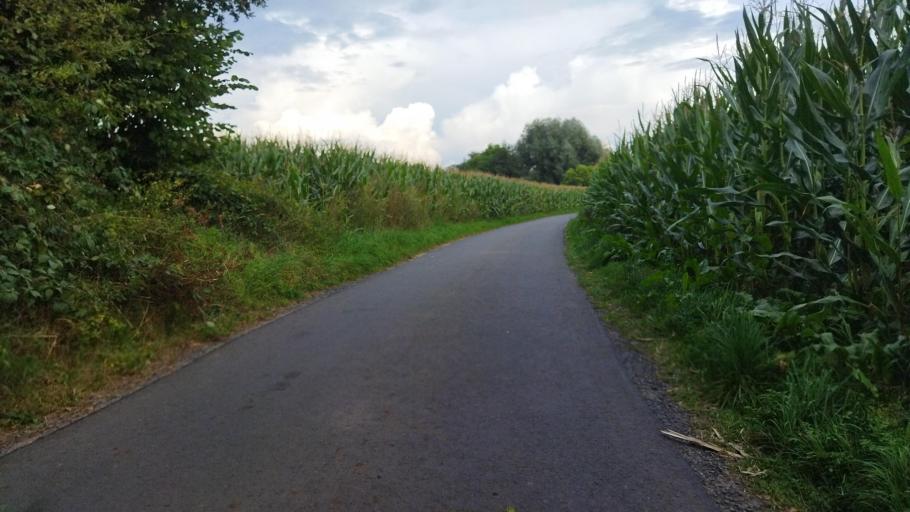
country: DE
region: North Rhine-Westphalia
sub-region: Regierungsbezirk Munster
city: Telgte
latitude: 52.0183
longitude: 7.7756
